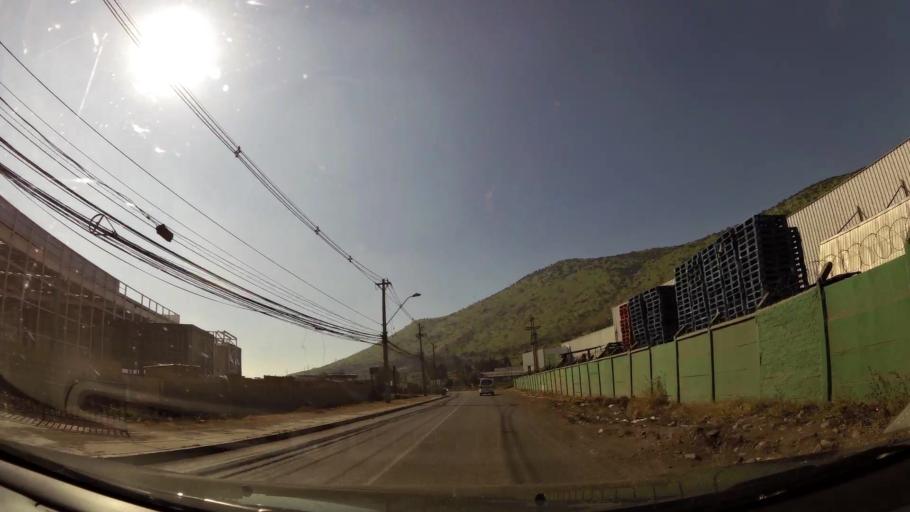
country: CL
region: Santiago Metropolitan
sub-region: Provincia de Chacabuco
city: Chicureo Abajo
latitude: -33.3343
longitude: -70.6970
